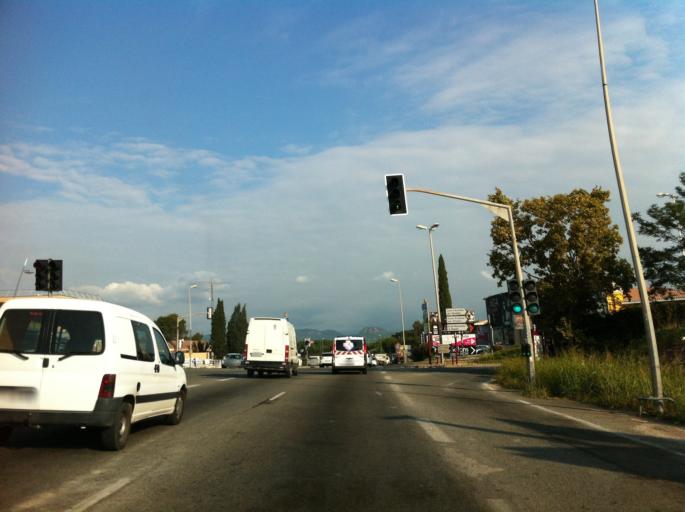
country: FR
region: Provence-Alpes-Cote d'Azur
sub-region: Departement du Var
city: Puget-sur-Argens
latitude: 43.4524
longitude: 6.6917
